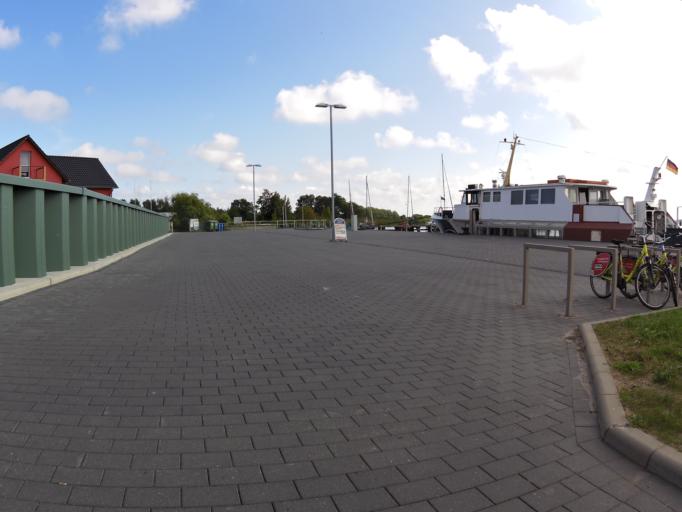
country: DE
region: Mecklenburg-Vorpommern
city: Kroslin
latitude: 54.1346
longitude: 13.7679
